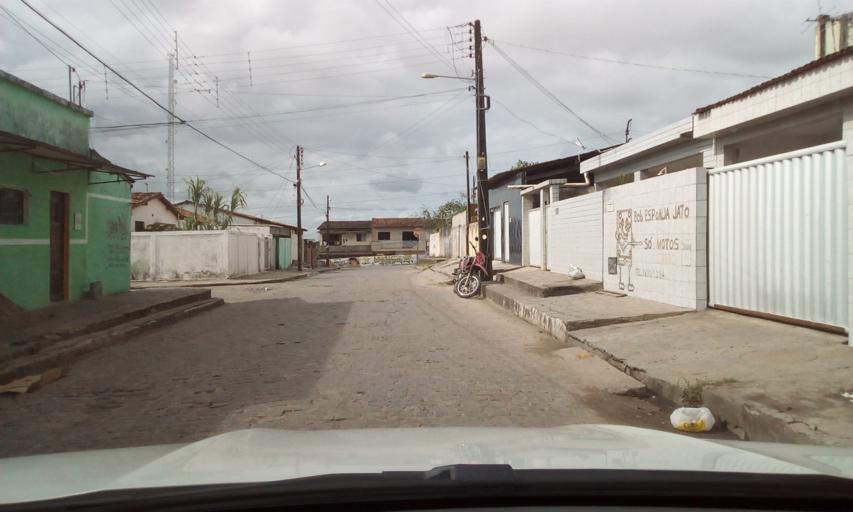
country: BR
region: Paraiba
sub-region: Joao Pessoa
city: Joao Pessoa
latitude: -7.1855
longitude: -34.8838
